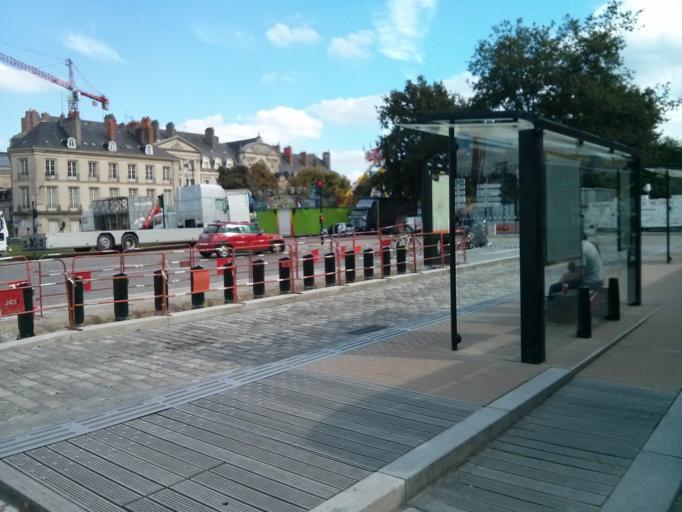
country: FR
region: Pays de la Loire
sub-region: Departement de la Loire-Atlantique
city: Nantes
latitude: 47.2194
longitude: -1.5505
